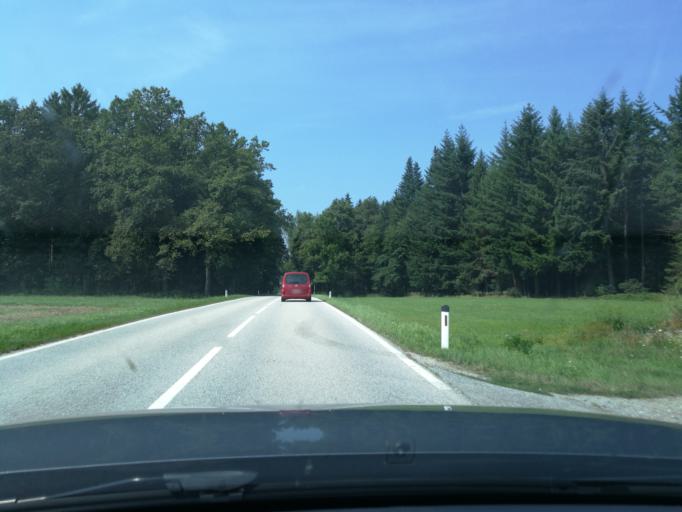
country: AT
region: Upper Austria
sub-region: Politischer Bezirk Grieskirchen
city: Grieskirchen
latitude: 48.3508
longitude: 13.7225
